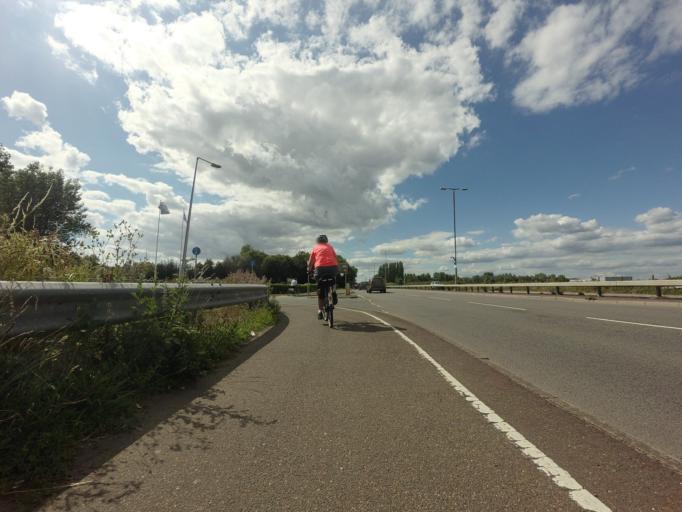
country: GB
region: England
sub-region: East Sussex
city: Eastbourne
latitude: 50.7922
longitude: 0.2928
